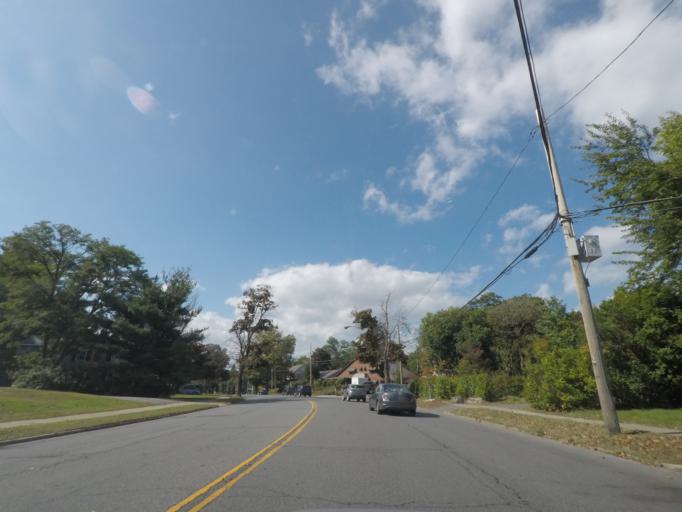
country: US
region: New York
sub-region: Albany County
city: Roessleville
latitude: 42.6593
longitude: -73.8087
